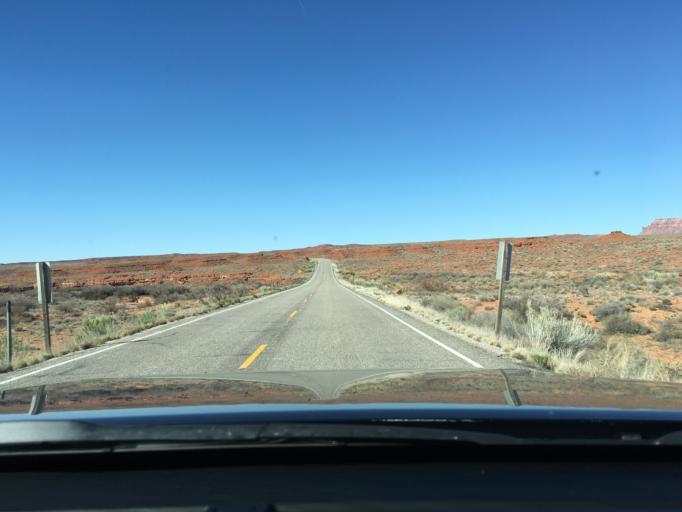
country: US
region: Utah
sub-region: San Juan County
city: Blanding
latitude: 37.2148
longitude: -109.8403
